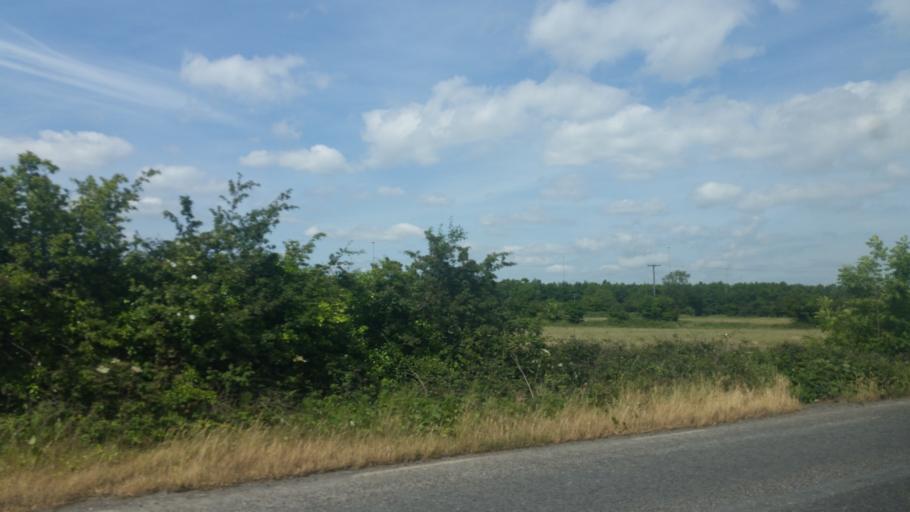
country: IE
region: Leinster
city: Balrothery
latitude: 53.5600
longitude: -6.2105
